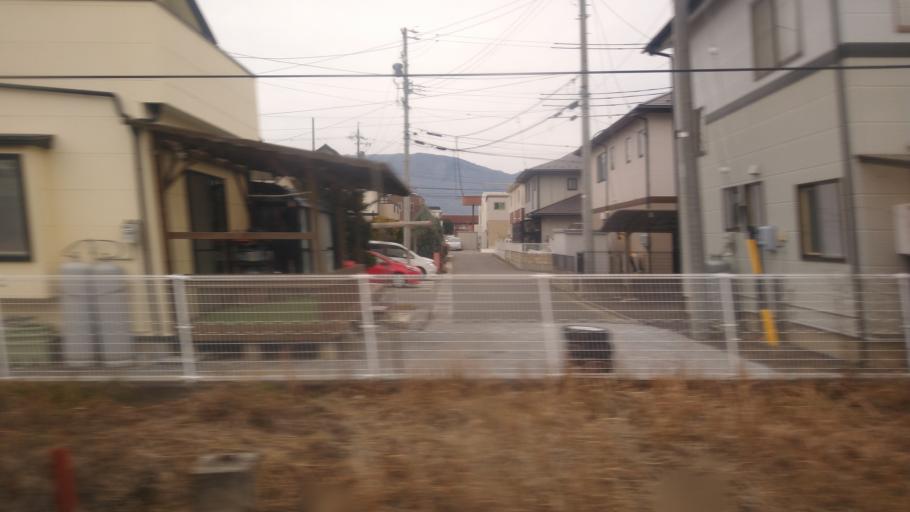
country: JP
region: Nagano
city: Shiojiri
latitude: 36.1268
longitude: 137.9485
